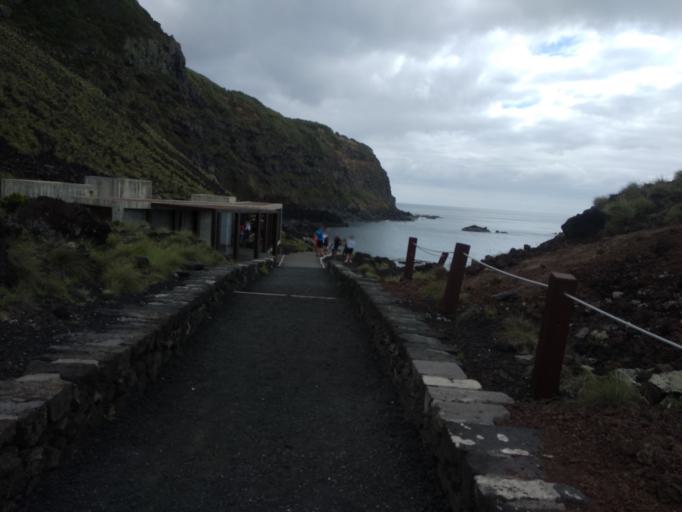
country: PT
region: Azores
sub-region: Ponta Delgada
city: Arrifes
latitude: 37.8597
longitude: -25.8526
